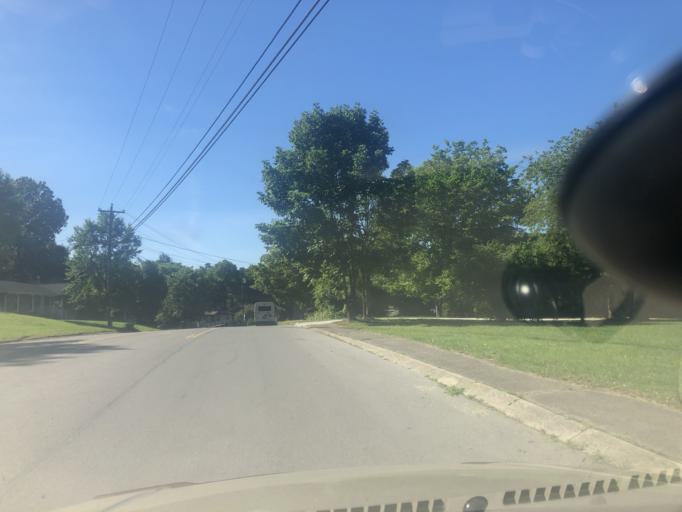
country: US
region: Tennessee
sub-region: Davidson County
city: Lakewood
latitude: 36.2487
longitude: -86.6697
